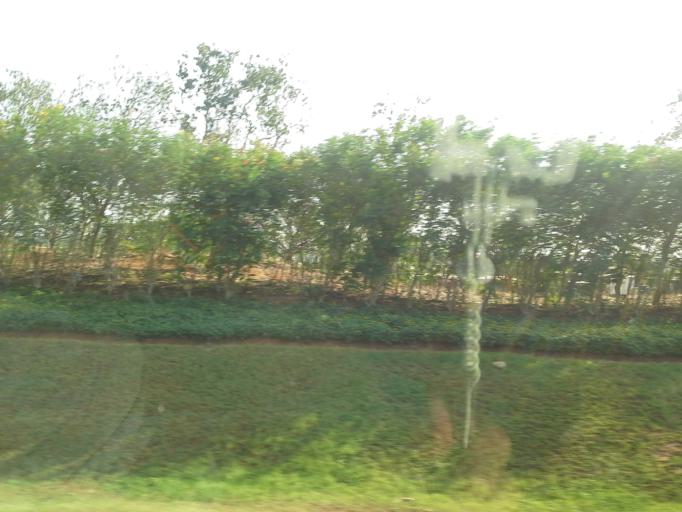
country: IN
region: Telangana
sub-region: Rangareddi
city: Balapur
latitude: 17.2450
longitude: 78.4020
